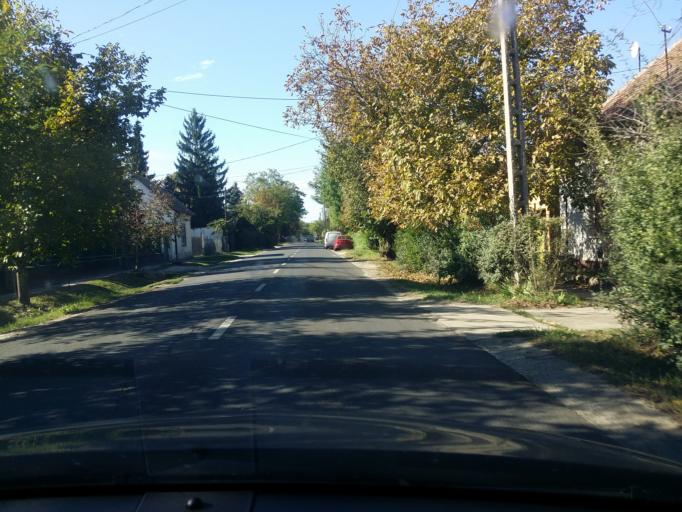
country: HU
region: Pest
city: God
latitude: 47.7014
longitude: 19.1493
